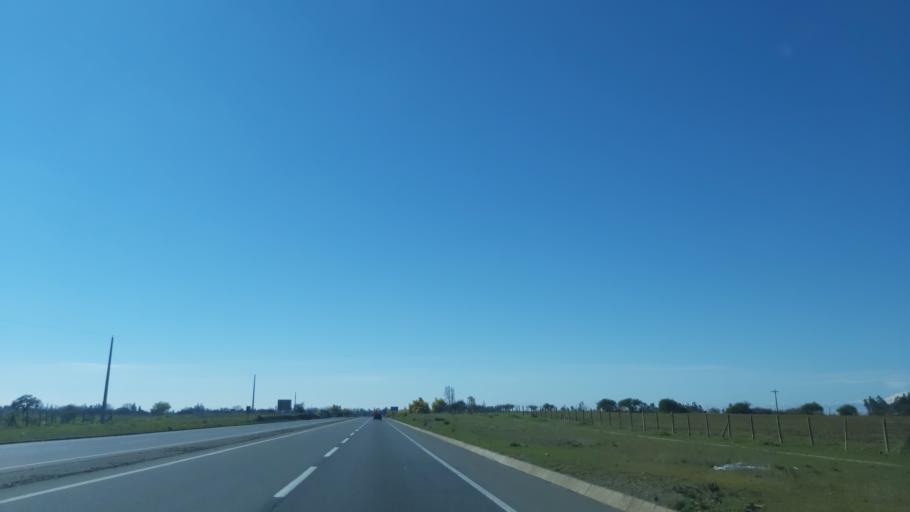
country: CL
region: Biobio
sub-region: Provincia de Nuble
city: Bulnes
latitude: -36.6568
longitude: -72.2465
